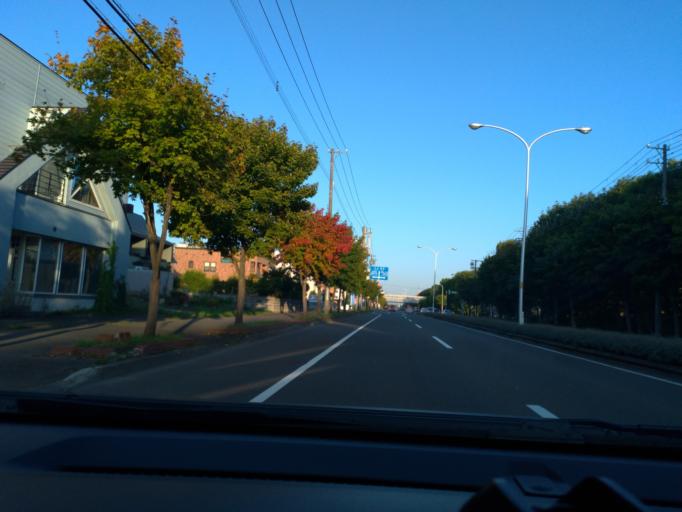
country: JP
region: Hokkaido
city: Ishikari
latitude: 43.1585
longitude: 141.3953
